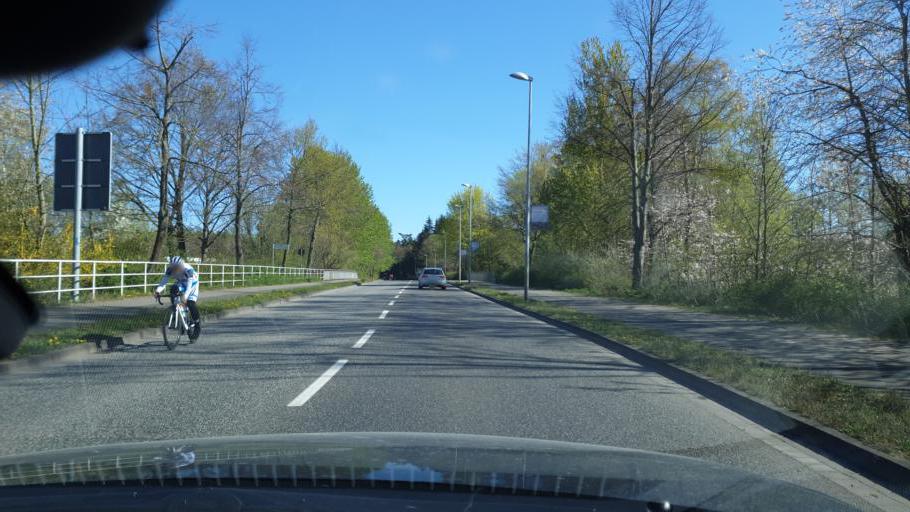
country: DE
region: Mecklenburg-Vorpommern
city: Werdervorstadt
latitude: 53.6455
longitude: 11.4271
